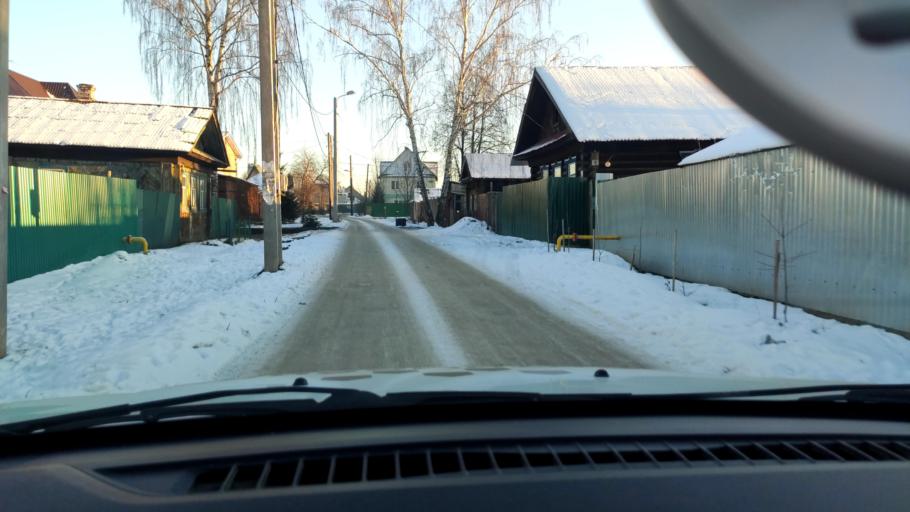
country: RU
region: Perm
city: Perm
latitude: 58.0505
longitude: 56.3307
